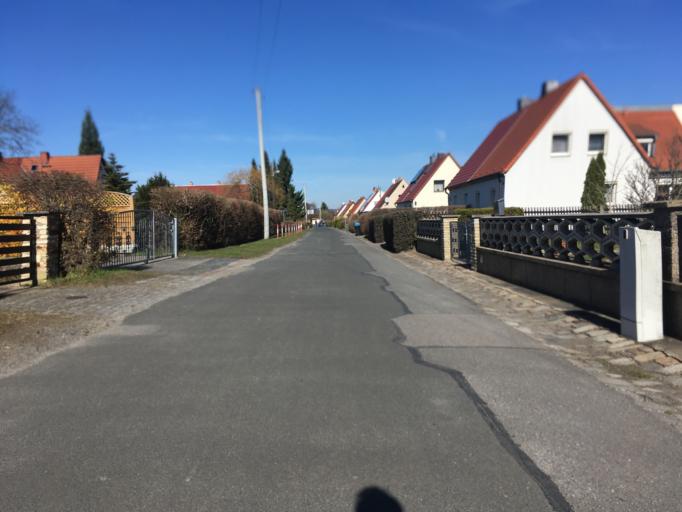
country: DE
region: Saxony
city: Radebeul
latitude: 51.0907
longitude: 13.6814
